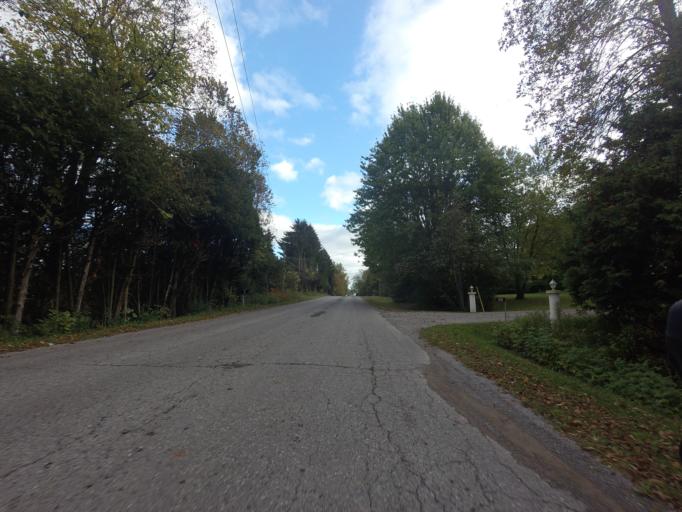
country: CA
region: Ontario
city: Cobourg
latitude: 43.9810
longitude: -77.9696
